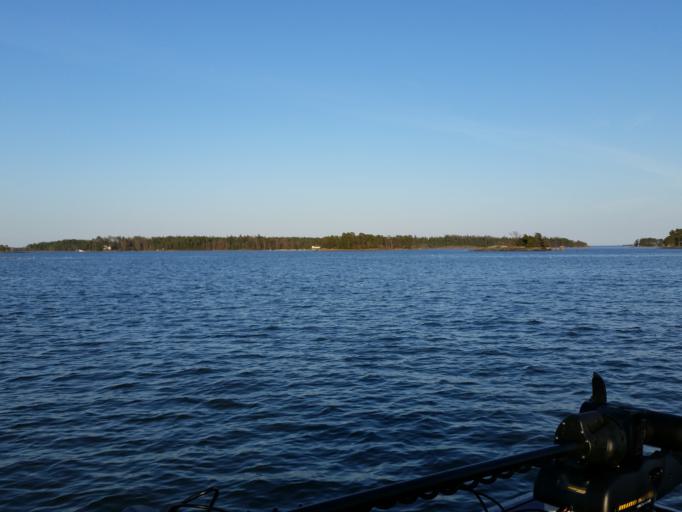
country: FI
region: Uusimaa
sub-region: Helsinki
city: Koukkuniemi
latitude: 60.1349
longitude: 24.7416
